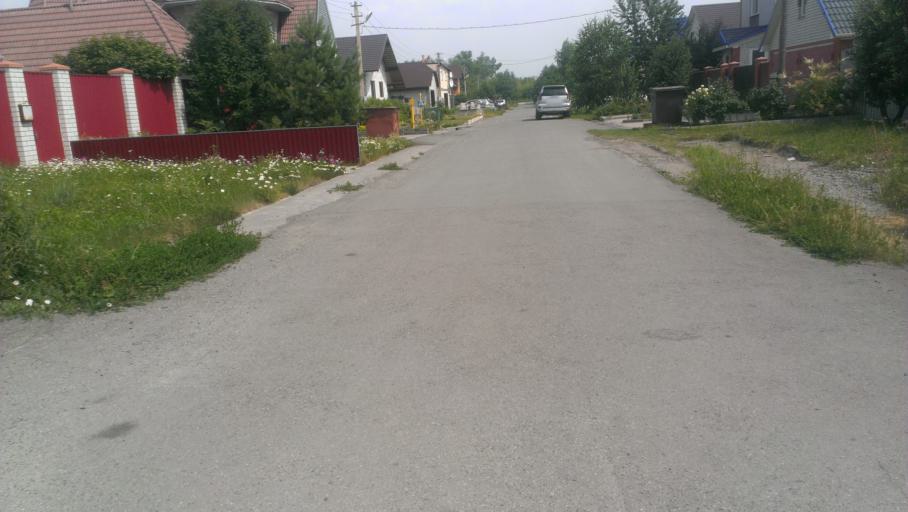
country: RU
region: Altai Krai
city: Novosilikatnyy
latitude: 53.3490
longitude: 83.6432
